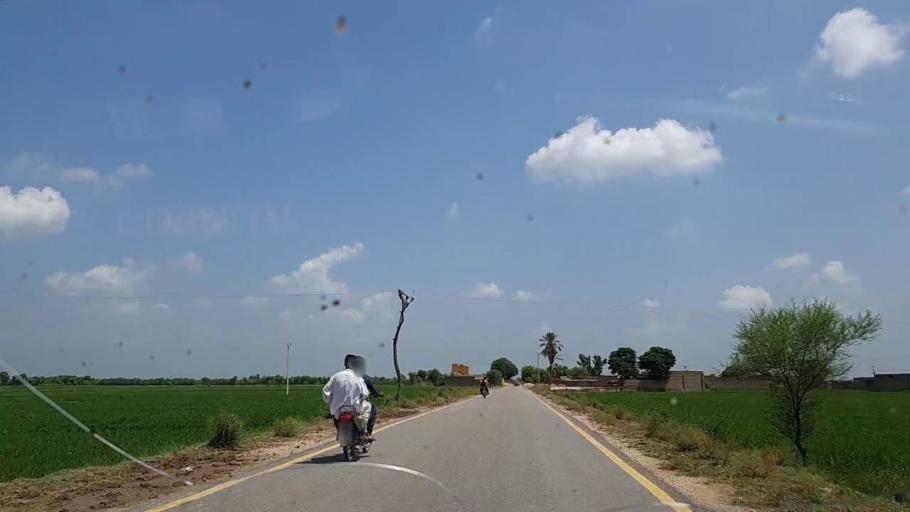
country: PK
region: Sindh
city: Tharu Shah
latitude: 26.9804
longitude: 68.0829
